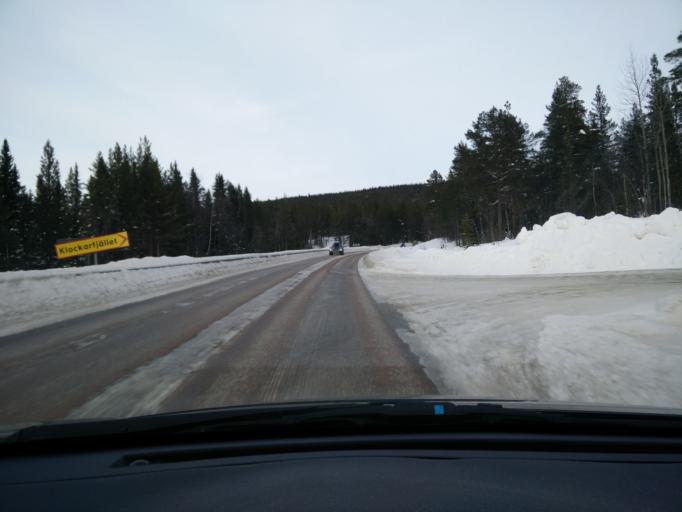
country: SE
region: Jaemtland
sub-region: Bergs Kommun
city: Hoverberg
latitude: 62.4933
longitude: 13.9288
